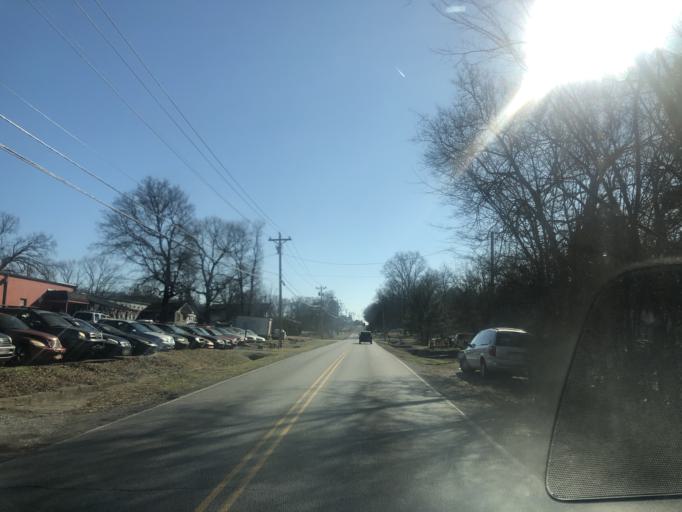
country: US
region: Tennessee
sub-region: Rutherford County
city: La Vergne
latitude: 35.9997
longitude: -86.5604
